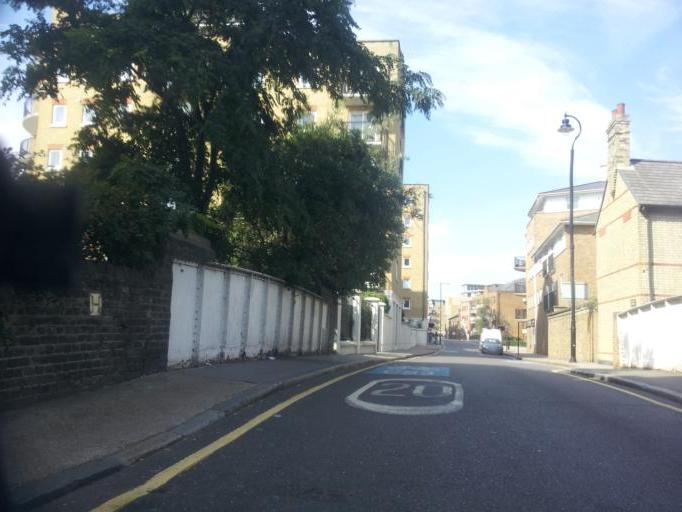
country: GB
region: England
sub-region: Greater London
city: Poplar
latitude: 51.5095
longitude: -0.0358
